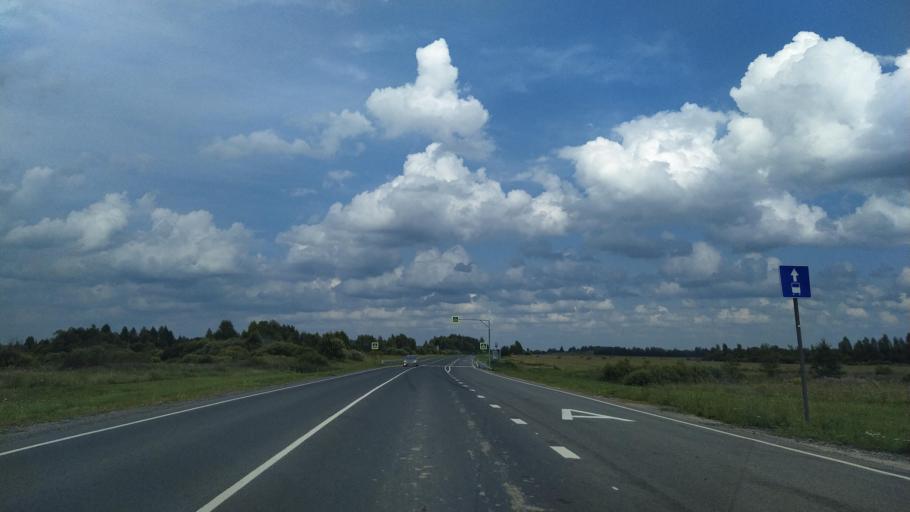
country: RU
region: Novgorod
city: Sol'tsy
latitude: 58.0764
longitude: 30.0685
